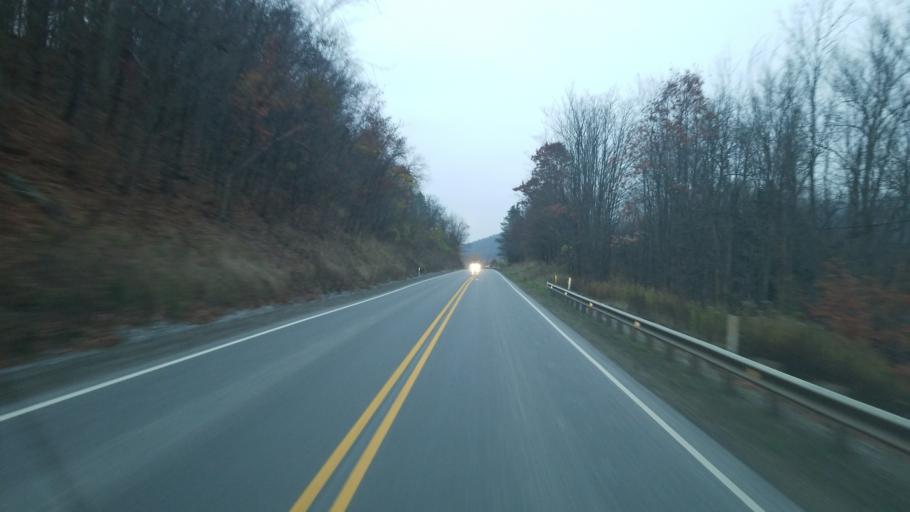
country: US
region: Pennsylvania
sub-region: McKean County
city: Smethport
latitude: 41.7890
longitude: -78.4150
